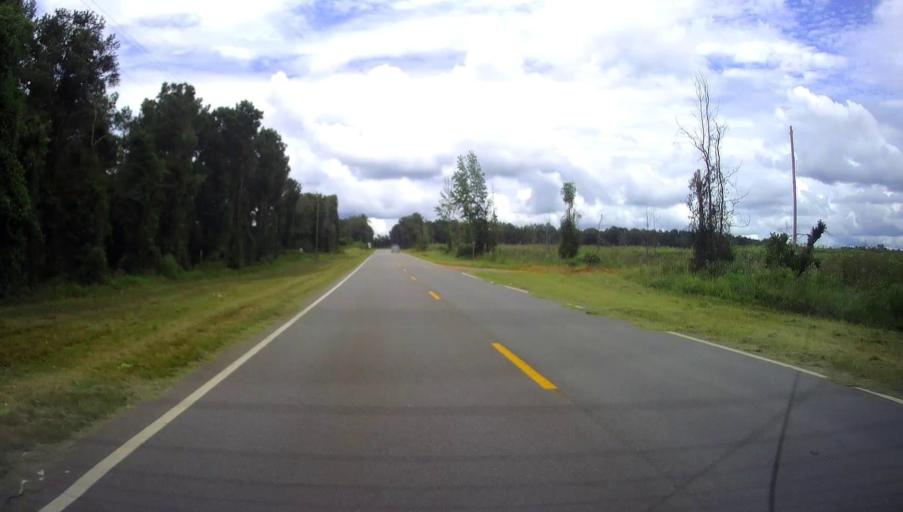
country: US
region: Georgia
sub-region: Schley County
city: Ellaville
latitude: 32.2642
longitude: -84.1947
